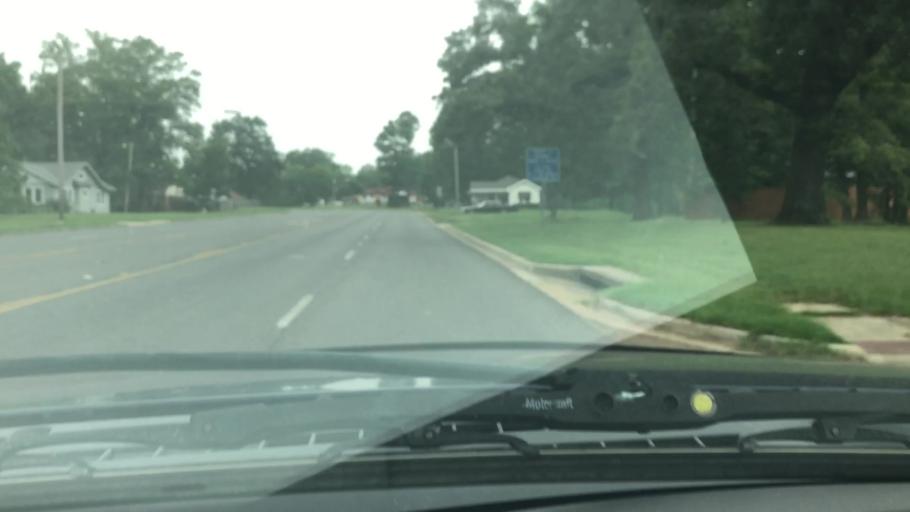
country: US
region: Texas
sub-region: Bowie County
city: Texarkana
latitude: 33.4308
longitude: -94.0616
